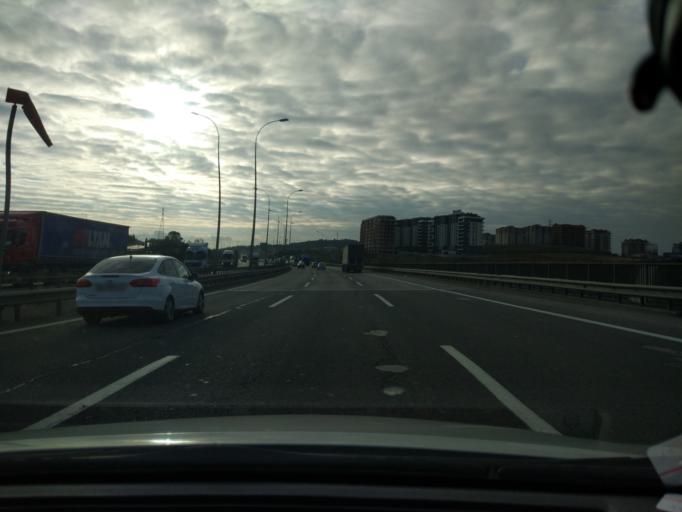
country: TR
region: Kocaeli
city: Balcik
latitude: 40.8407
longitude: 29.4151
